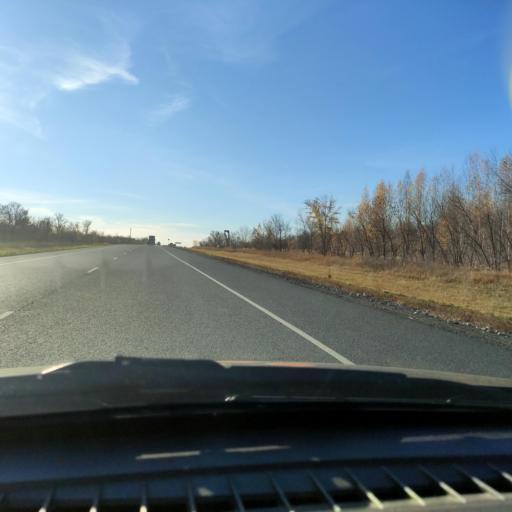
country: RU
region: Samara
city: Mezhdurechensk
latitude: 53.2394
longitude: 48.9638
